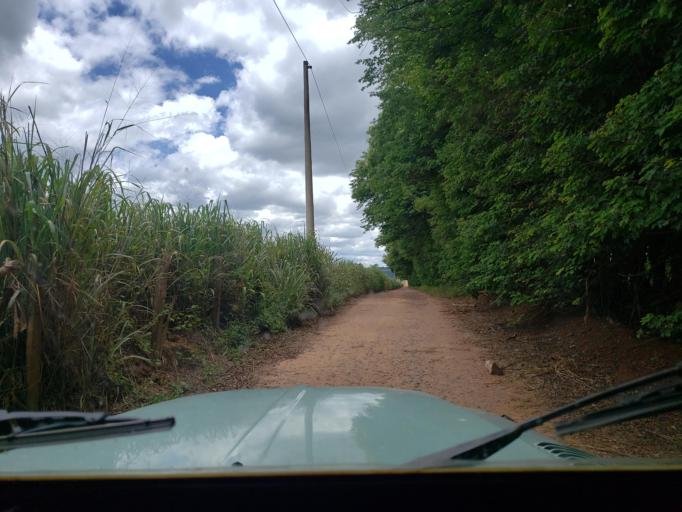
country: BR
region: Sao Paulo
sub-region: Moji-Guacu
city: Mogi-Gaucu
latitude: -22.2228
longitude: -46.8438
